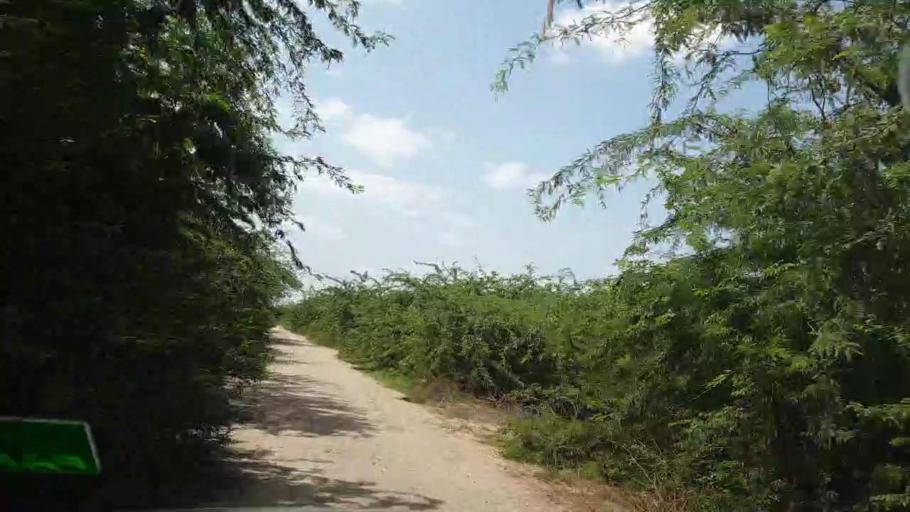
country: PK
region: Sindh
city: Kadhan
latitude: 24.5518
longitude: 69.1900
